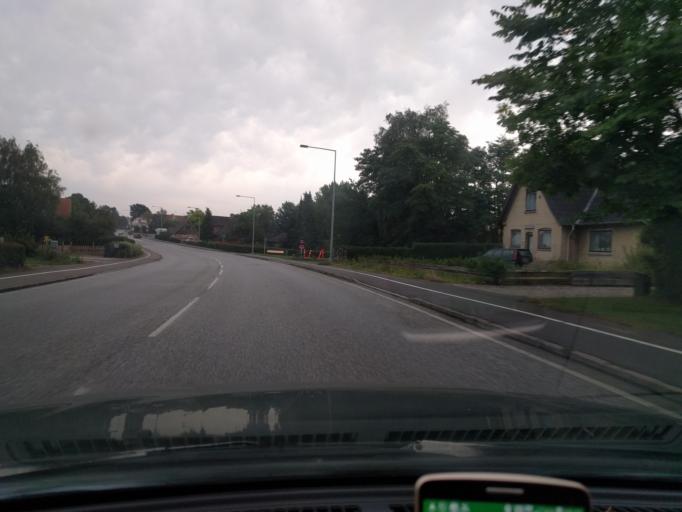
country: DK
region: Zealand
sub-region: Guldborgsund Kommune
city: Norre Alslev
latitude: 54.9020
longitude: 11.8726
